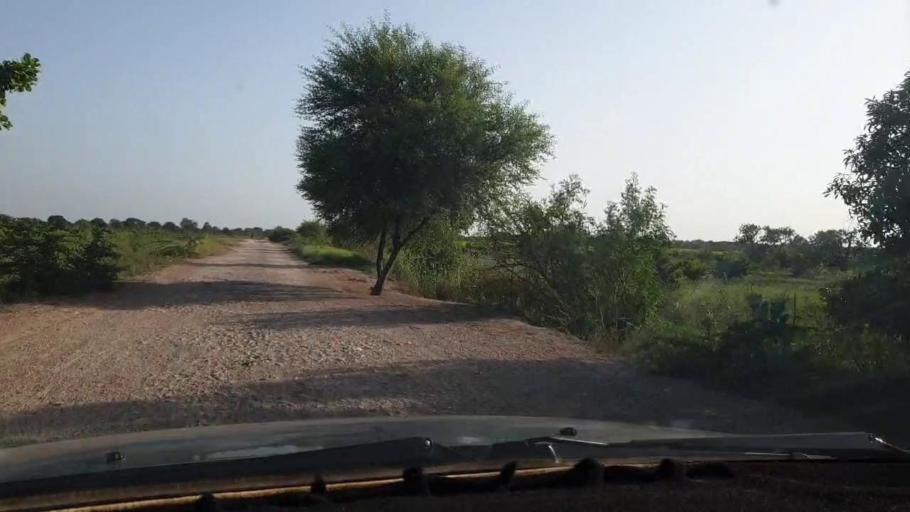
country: PK
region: Sindh
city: Mirwah Gorchani
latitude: 25.3012
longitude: 68.9643
